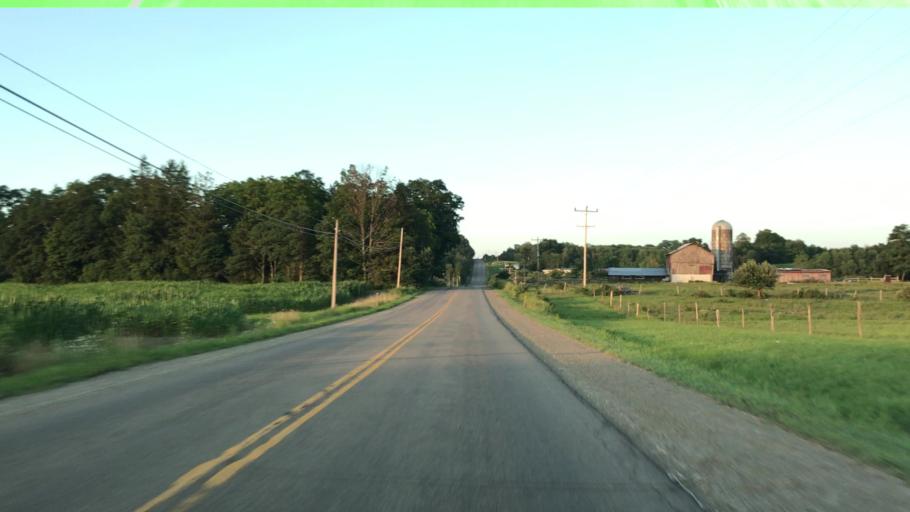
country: US
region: New York
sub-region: Chautauqua County
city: Mayville
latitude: 42.2755
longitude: -79.4540
